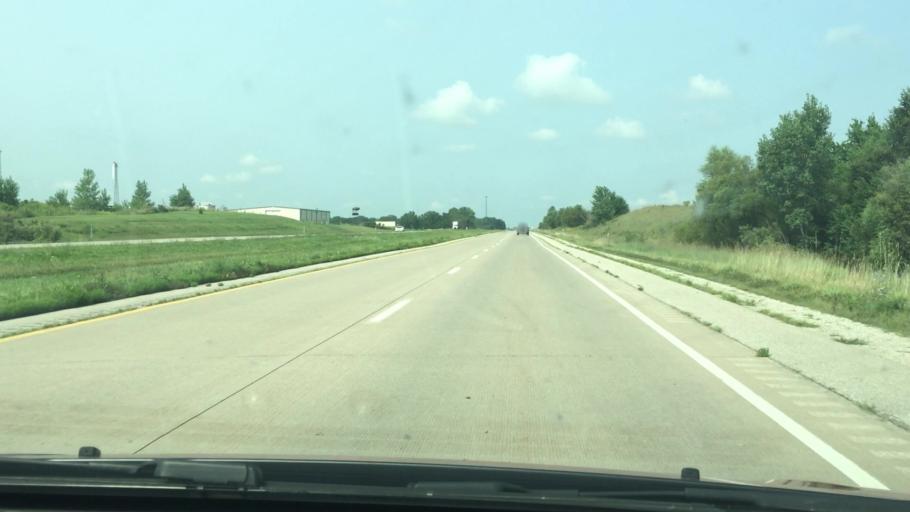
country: US
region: Iowa
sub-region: Scott County
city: Blue Grass
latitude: 41.5164
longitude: -90.8322
